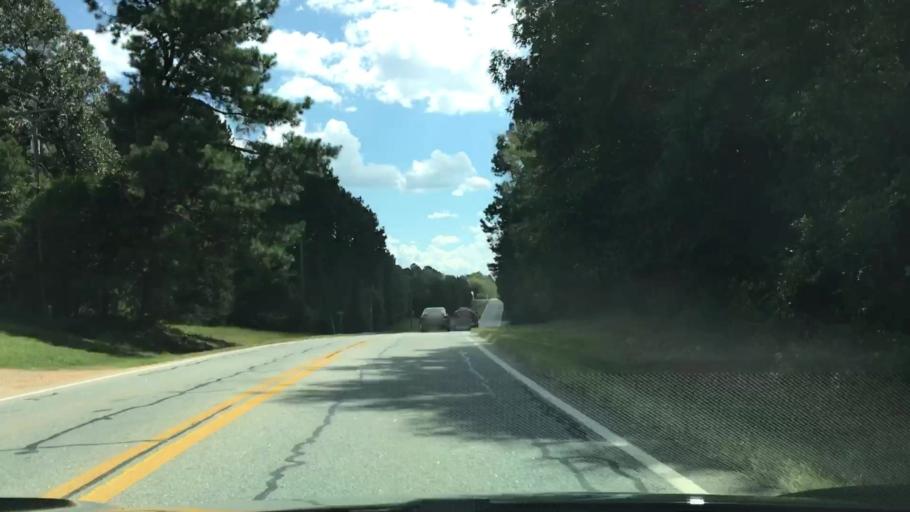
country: US
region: Georgia
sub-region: Oconee County
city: Watkinsville
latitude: 33.7798
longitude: -83.3115
